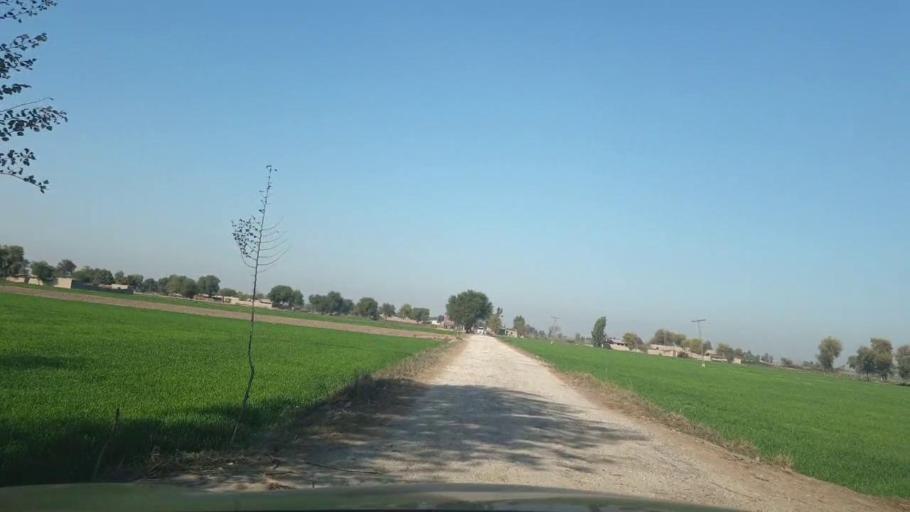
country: PK
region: Sindh
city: Mirpur Mathelo
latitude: 28.0011
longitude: 69.4795
